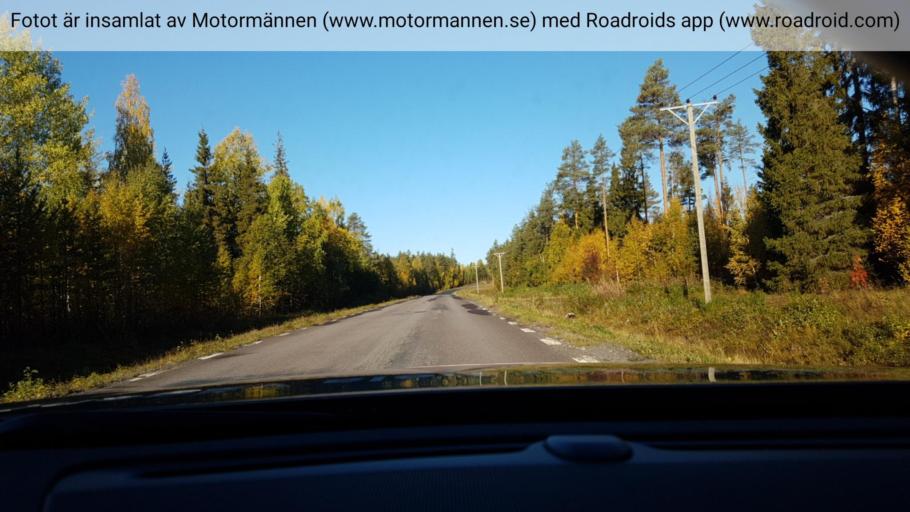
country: SE
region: Norrbotten
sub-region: Bodens Kommun
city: Boden
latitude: 65.9508
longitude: 21.6129
